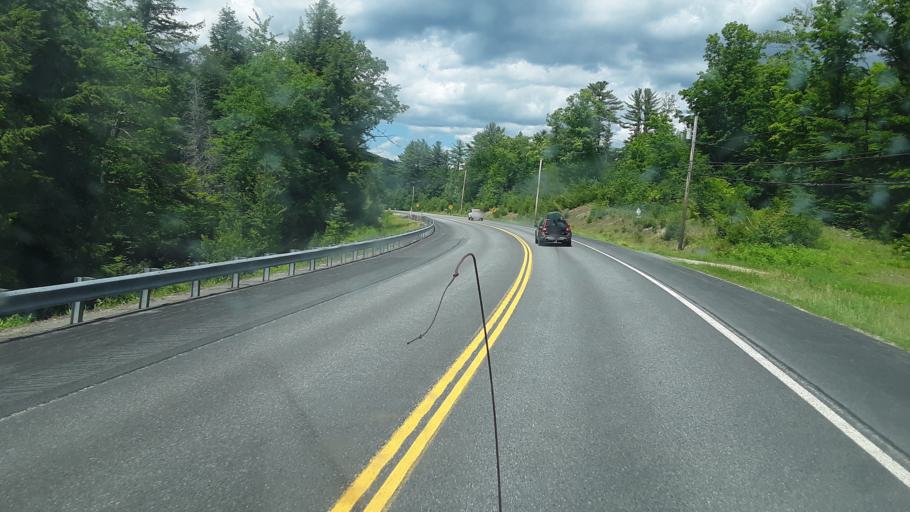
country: US
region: Maine
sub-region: Oxford County
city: Peru
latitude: 44.5373
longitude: -70.4051
